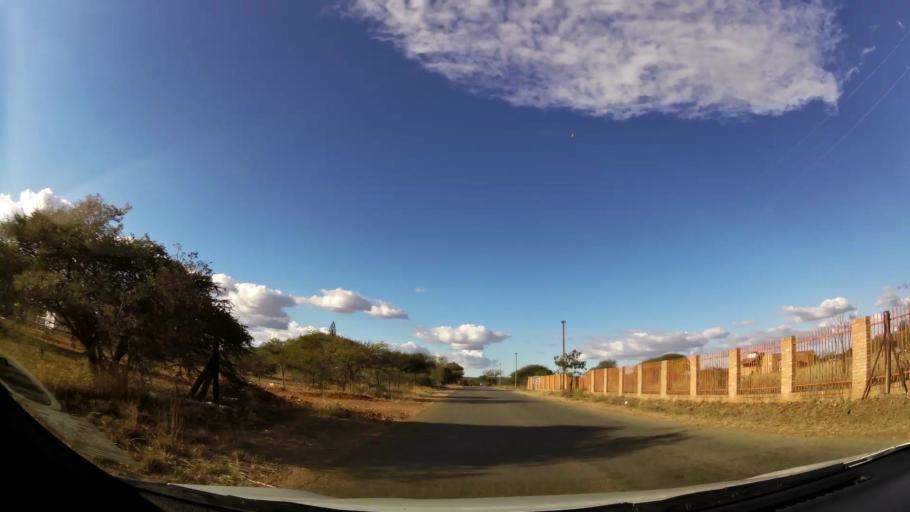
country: ZA
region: Limpopo
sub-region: Capricorn District Municipality
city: Polokwane
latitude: -23.9324
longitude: 29.4378
